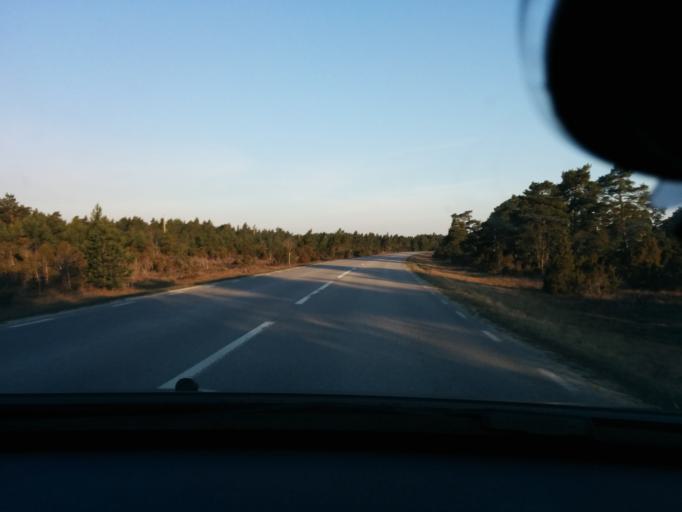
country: SE
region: Gotland
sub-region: Gotland
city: Visby
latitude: 57.6325
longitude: 18.4119
